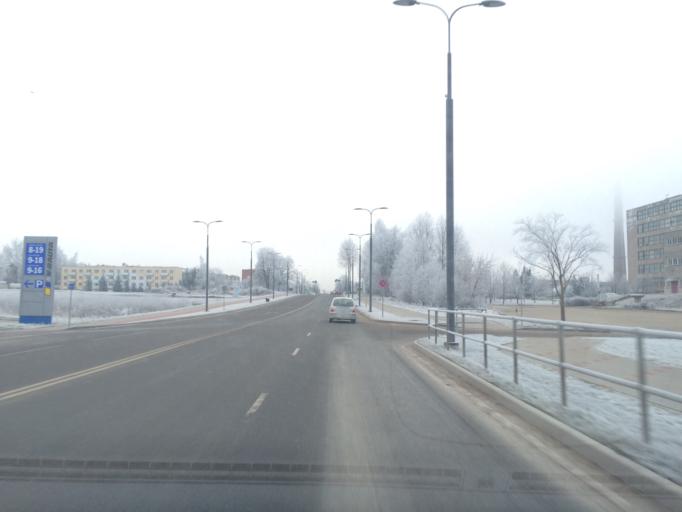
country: LV
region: Rezekne
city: Rezekne
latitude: 56.5320
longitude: 27.3463
